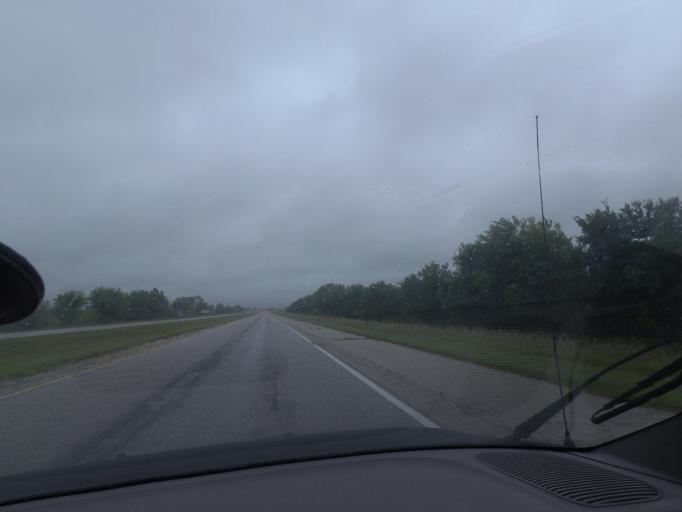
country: US
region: Illinois
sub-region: Pike County
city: Pittsfield
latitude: 39.6728
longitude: -90.8522
